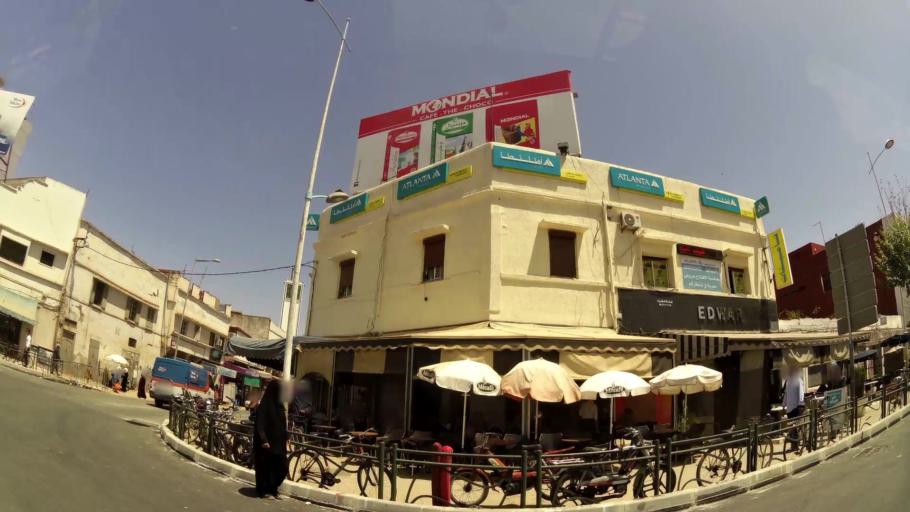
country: MA
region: Rabat-Sale-Zemmour-Zaer
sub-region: Khemisset
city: Khemisset
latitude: 33.8260
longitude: -6.0710
